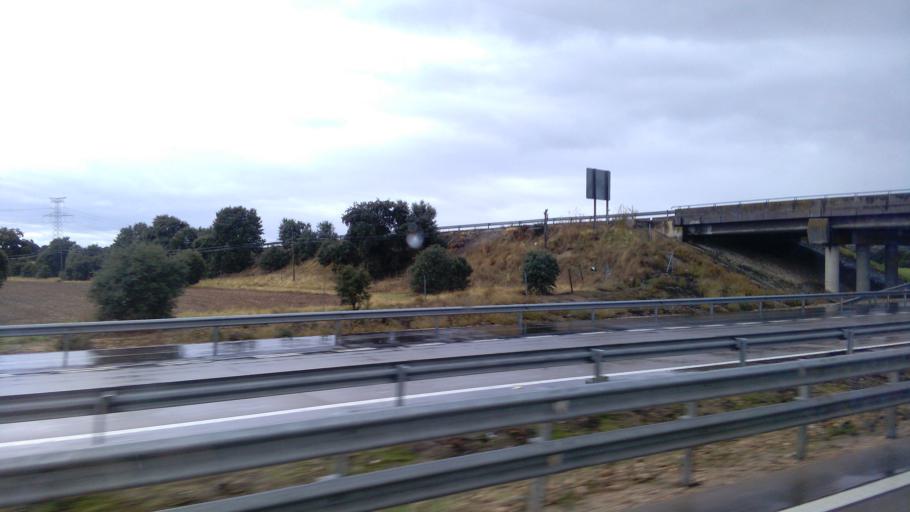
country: ES
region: Castille-La Mancha
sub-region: Province of Toledo
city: Cervera de los Montes
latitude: 40.0121
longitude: -4.7789
